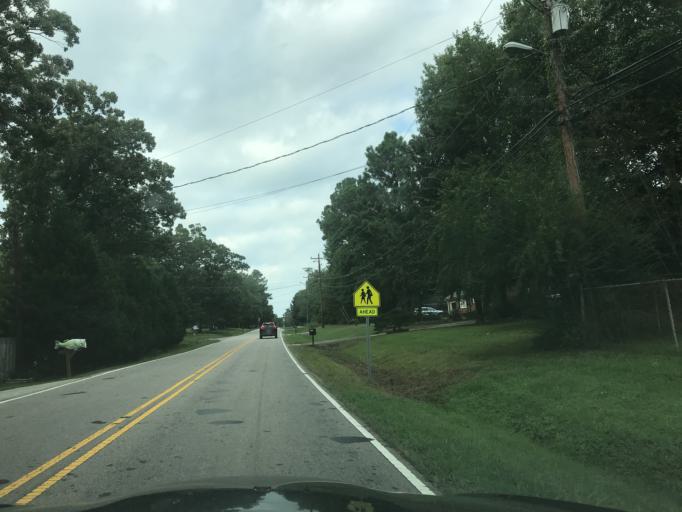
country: US
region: North Carolina
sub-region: Durham County
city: Durham
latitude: 35.9286
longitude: -78.9107
